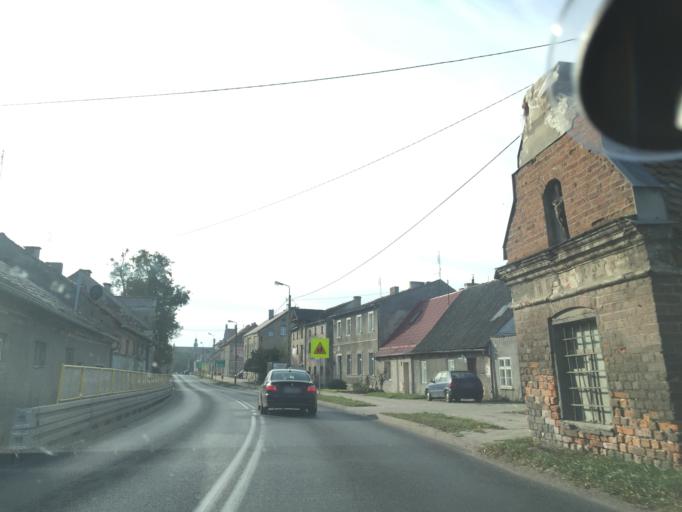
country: PL
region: Warmian-Masurian Voivodeship
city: Dobre Miasto
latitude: 53.9920
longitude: 20.3944
